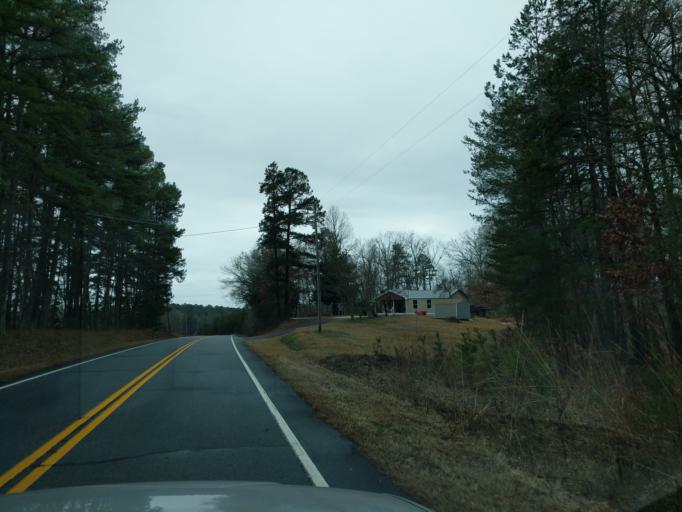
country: US
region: South Carolina
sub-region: Oconee County
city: Walhalla
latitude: 34.7999
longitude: -83.0769
